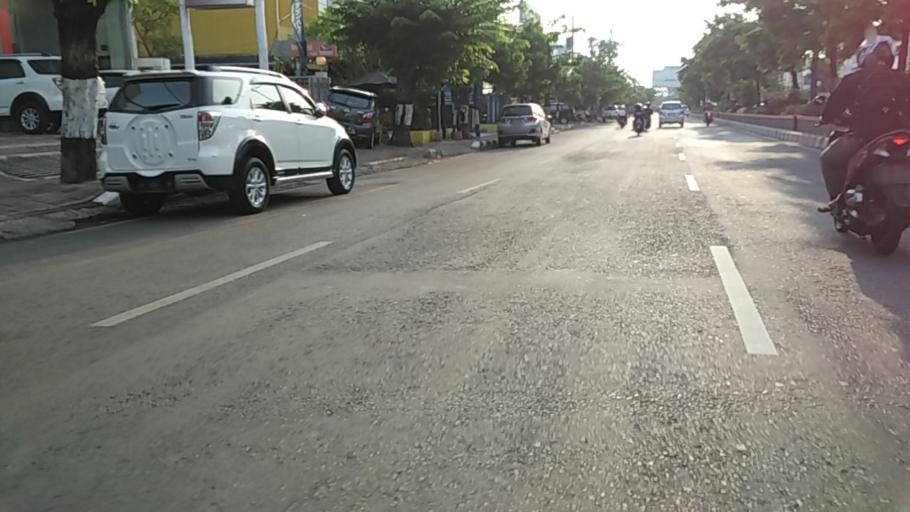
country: ID
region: Central Java
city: Semarang
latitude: -6.9813
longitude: 110.3971
